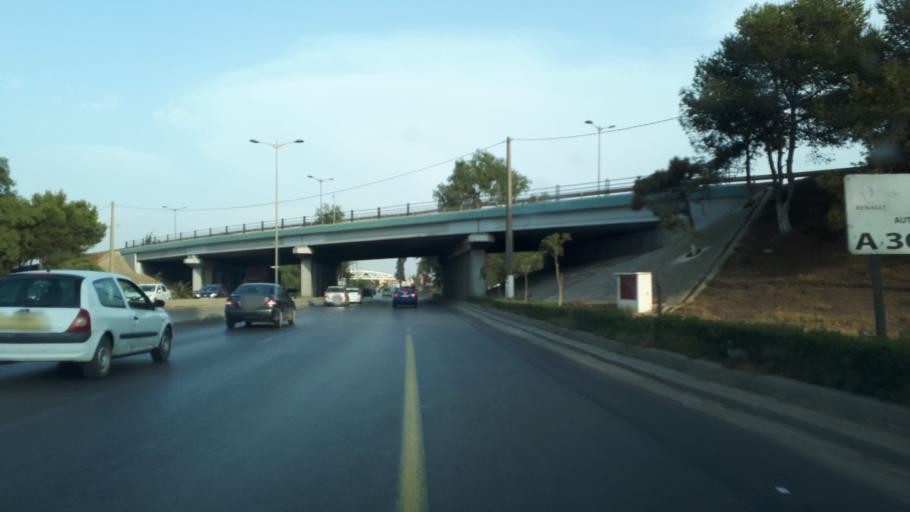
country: DZ
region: Alger
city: Dar el Beida
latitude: 36.7278
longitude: 3.2105
